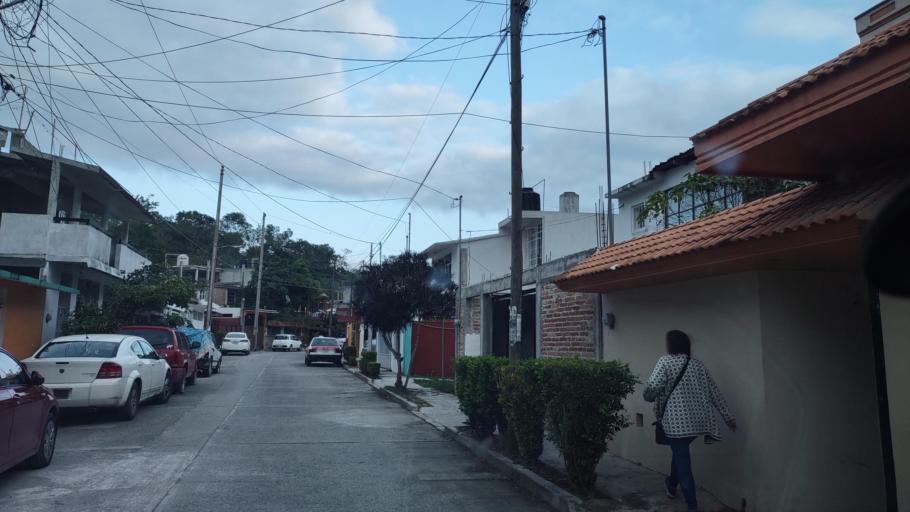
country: MX
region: Veracruz
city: Papantla de Olarte
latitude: 20.4552
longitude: -97.3077
